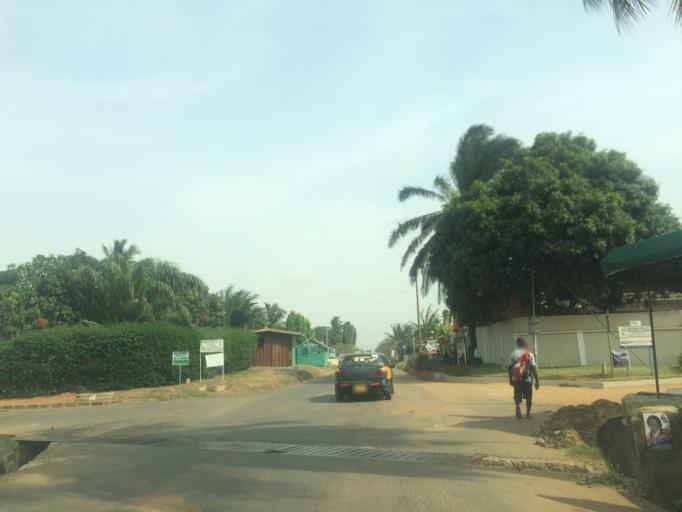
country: GH
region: Greater Accra
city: Nungua
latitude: 5.5997
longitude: -0.0910
